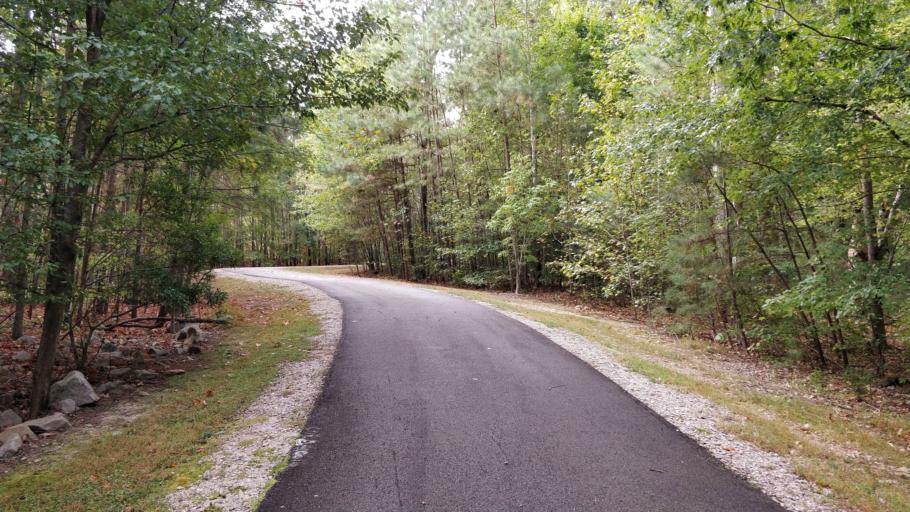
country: US
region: North Carolina
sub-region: Wake County
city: West Raleigh
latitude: 35.9087
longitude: -78.6693
